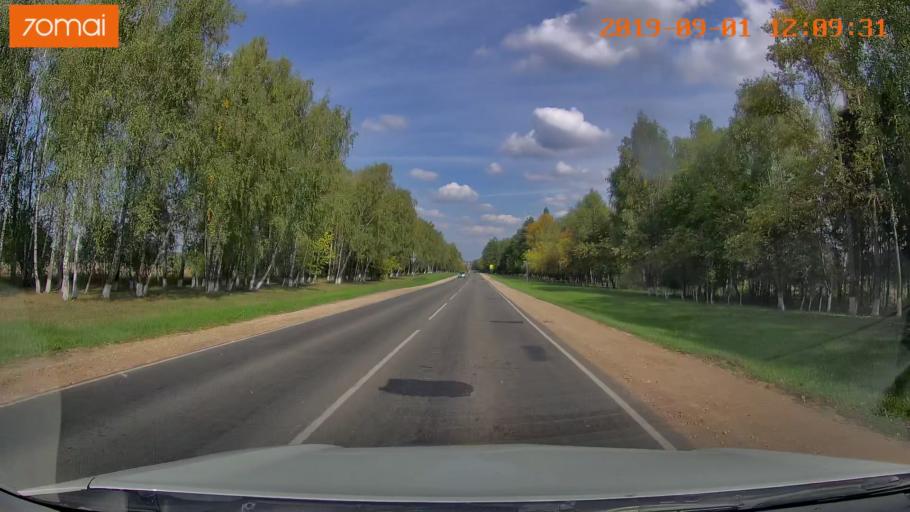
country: RU
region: Kaluga
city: Maloyaroslavets
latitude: 54.9814
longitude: 36.4266
